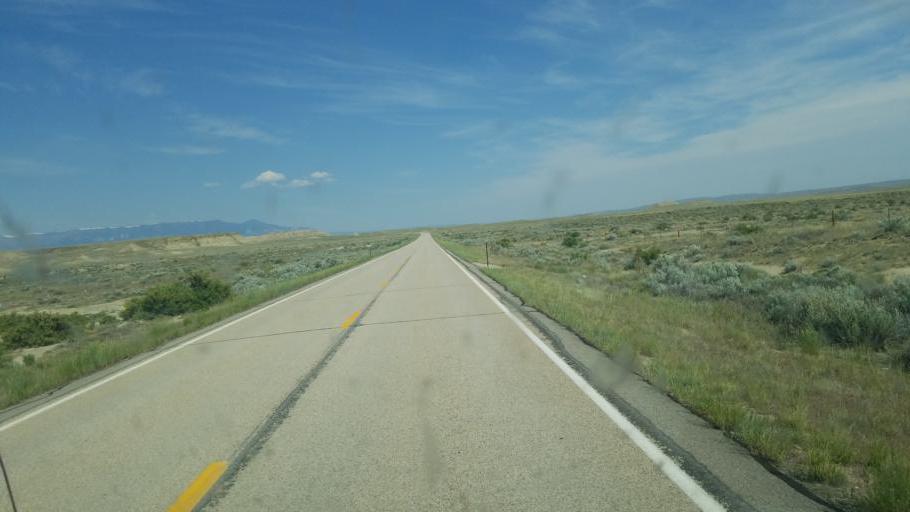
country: US
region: Wyoming
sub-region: Park County
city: Powell
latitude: 44.8247
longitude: -108.9759
